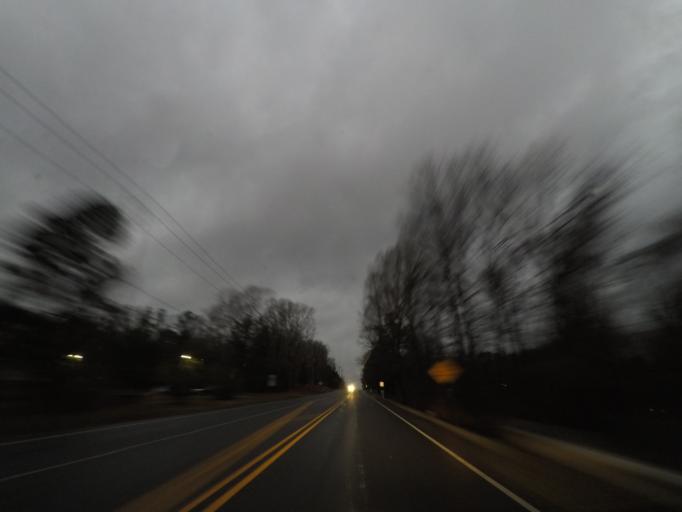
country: US
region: North Carolina
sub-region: Orange County
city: Hillsborough
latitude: 36.0928
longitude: -79.1046
